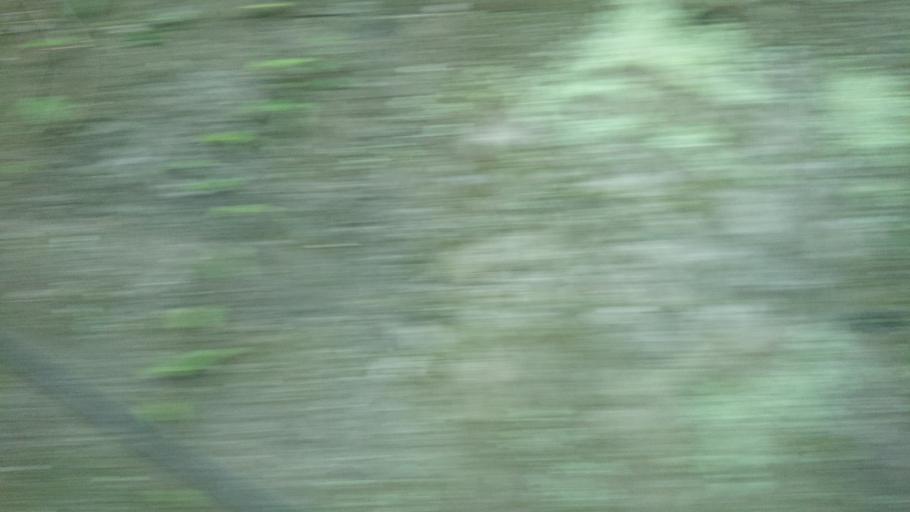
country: TW
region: Taiwan
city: Daxi
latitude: 24.8804
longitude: 121.3808
